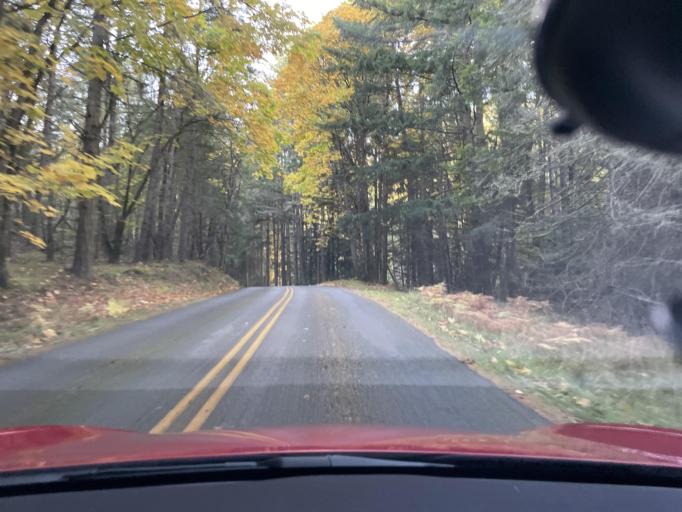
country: US
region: Washington
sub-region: San Juan County
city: Friday Harbor
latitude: 48.5247
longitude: -123.1458
